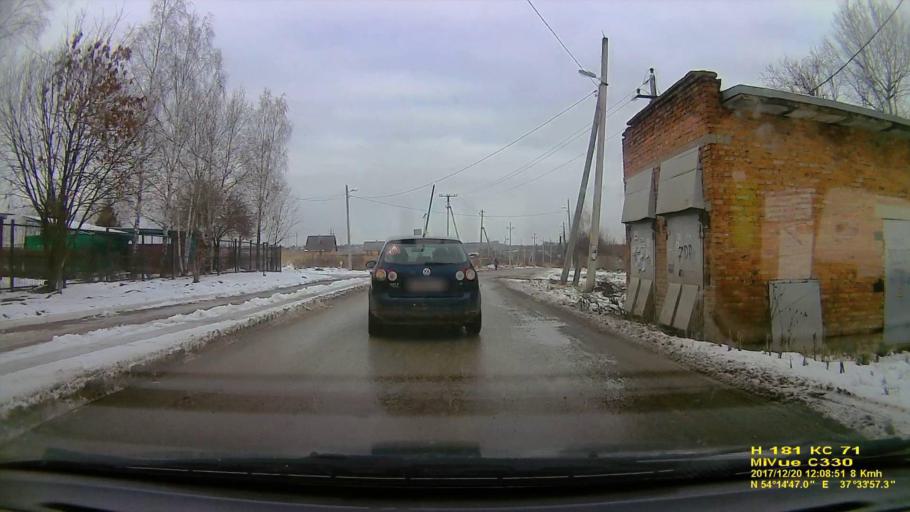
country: RU
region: Tula
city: Gorelki
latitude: 54.2464
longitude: 37.5660
